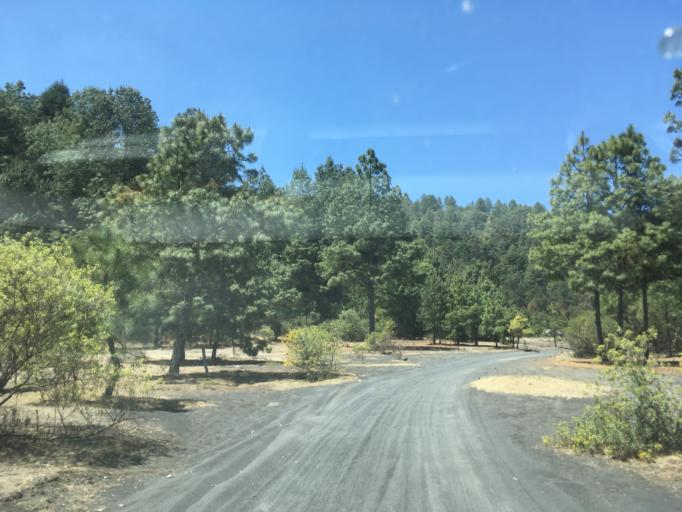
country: MX
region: Michoacan
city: Angahuan
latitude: 19.4788
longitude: -102.2468
